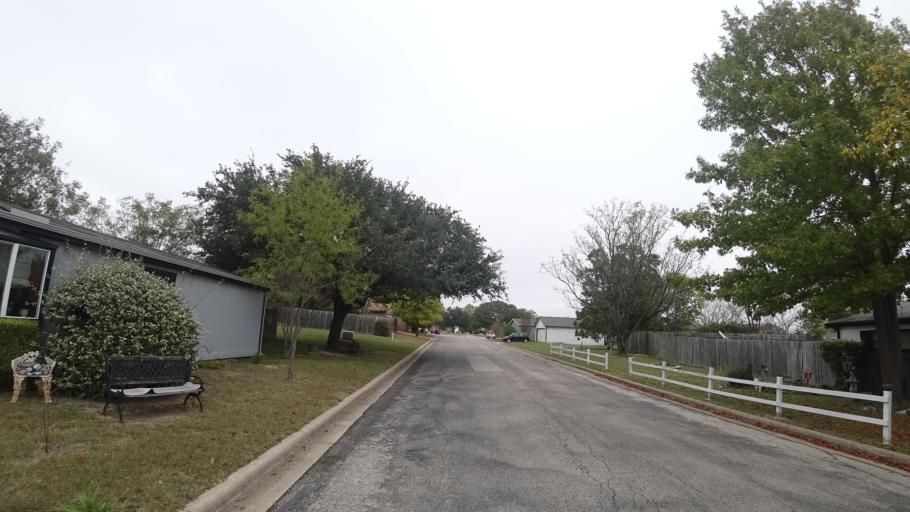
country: US
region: Texas
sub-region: Travis County
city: Pflugerville
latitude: 30.3913
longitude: -97.6426
